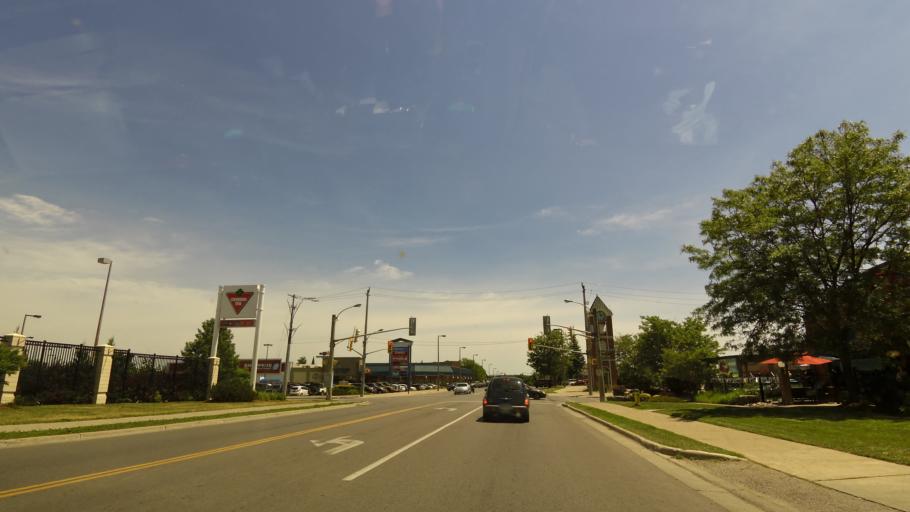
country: CA
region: Ontario
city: Ingersoll
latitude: 42.8636
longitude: -80.7310
